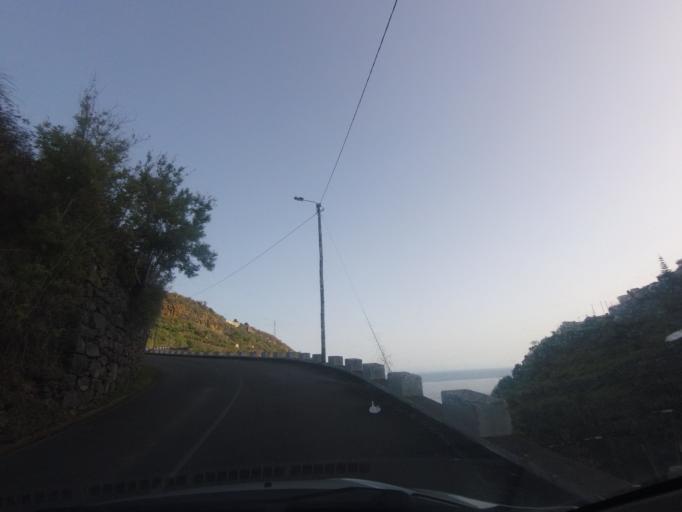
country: PT
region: Madeira
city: Ponta do Sol
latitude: 32.6874
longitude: -17.0830
